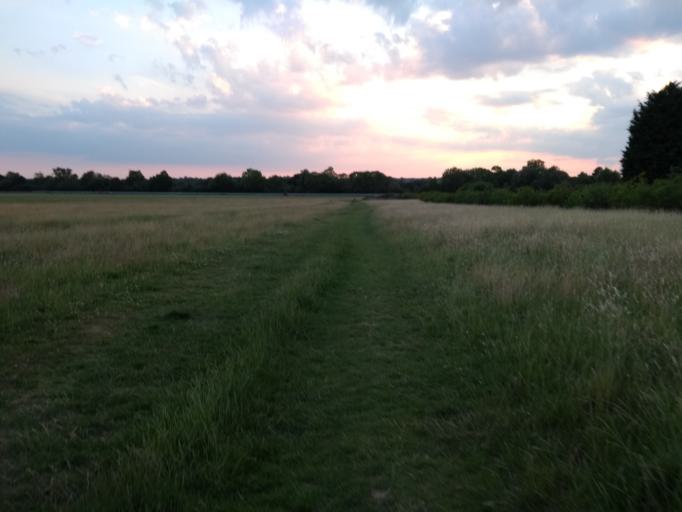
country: GB
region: England
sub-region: Warwickshire
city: Warwick
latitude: 52.2813
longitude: -1.6004
